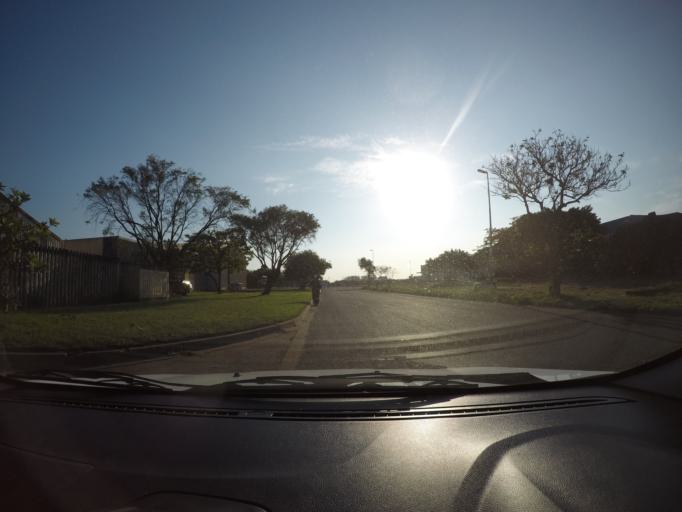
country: ZA
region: KwaZulu-Natal
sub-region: uThungulu District Municipality
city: Richards Bay
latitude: -28.7635
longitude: 32.0054
